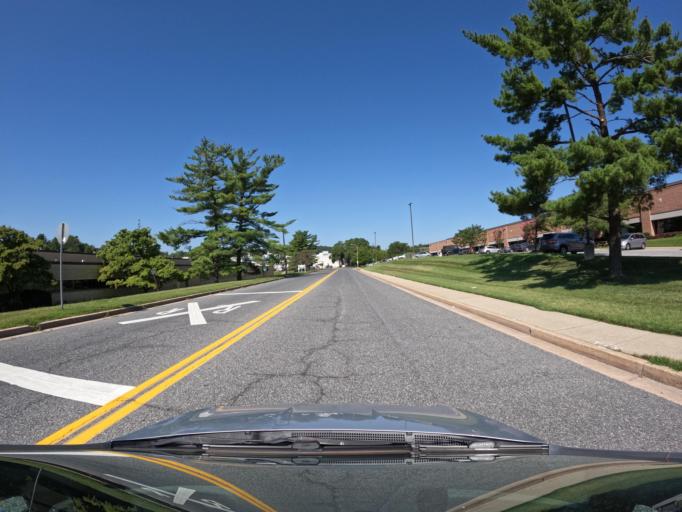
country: US
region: Maryland
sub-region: Baltimore County
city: Cockeysville
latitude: 39.4893
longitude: -76.6618
